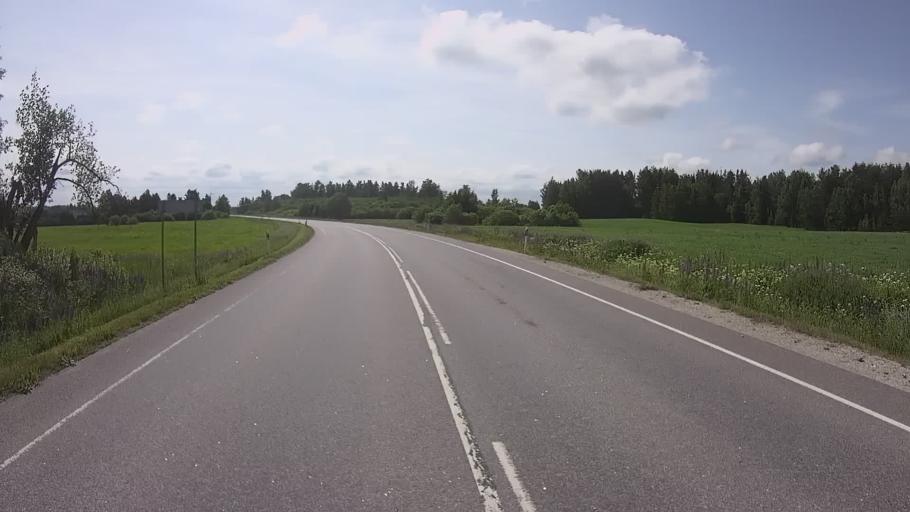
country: EE
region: Tartu
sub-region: UElenurme vald
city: Ulenurme
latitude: 58.2247
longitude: 26.7870
